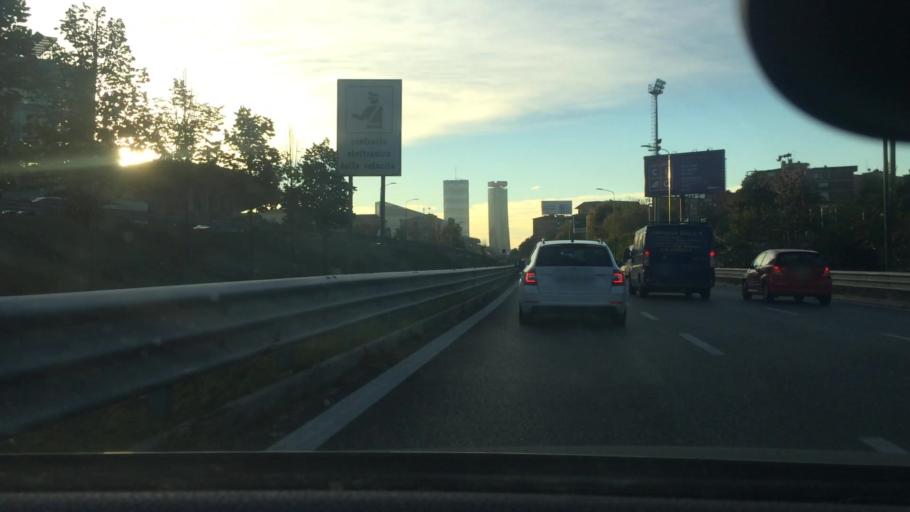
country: IT
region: Lombardy
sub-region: Citta metropolitana di Milano
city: Novate Milanese
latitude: 45.4906
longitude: 9.1383
